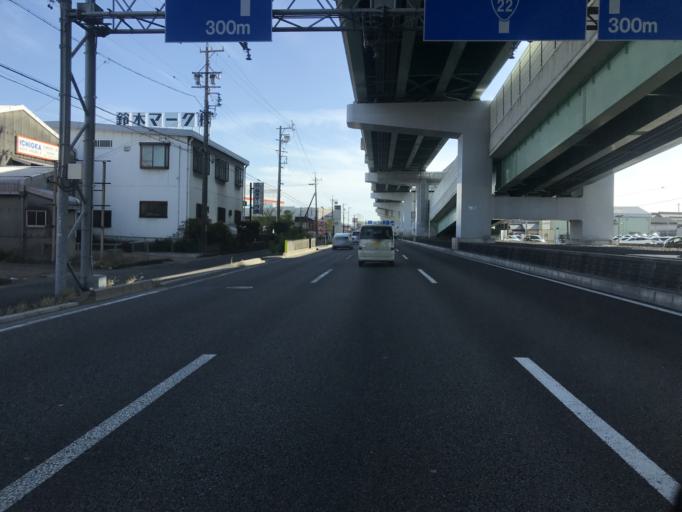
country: JP
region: Aichi
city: Iwakura
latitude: 35.2327
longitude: 136.8506
